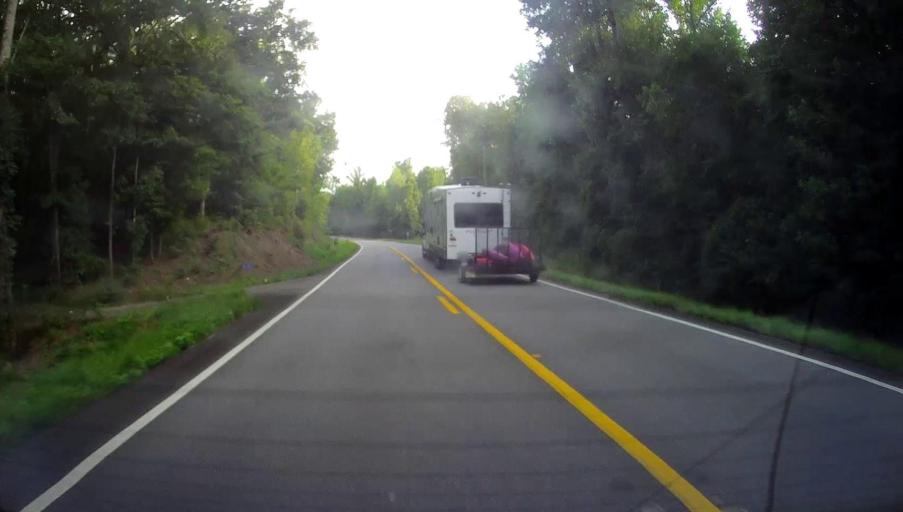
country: US
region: Georgia
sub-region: Crawford County
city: Knoxville
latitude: 32.8843
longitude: -83.9959
